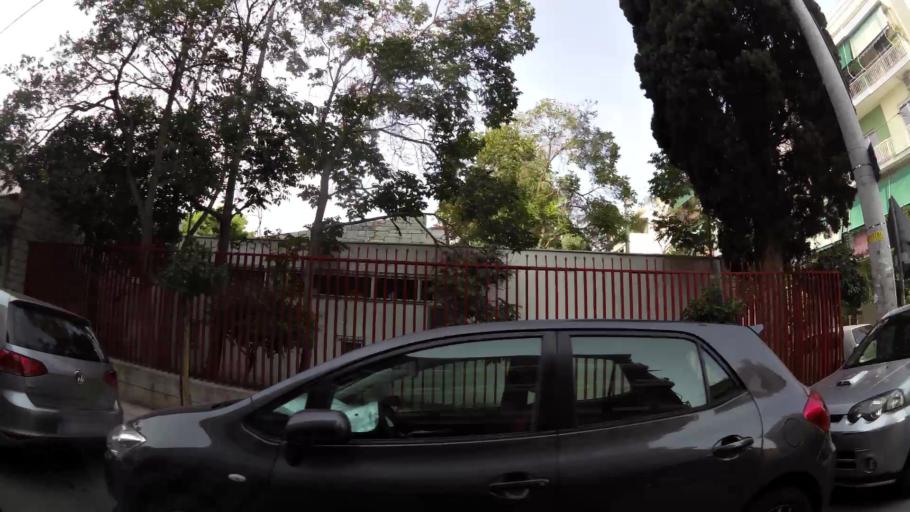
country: GR
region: Attica
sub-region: Nomarchia Athinas
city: Kallithea
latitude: 37.9572
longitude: 23.6985
